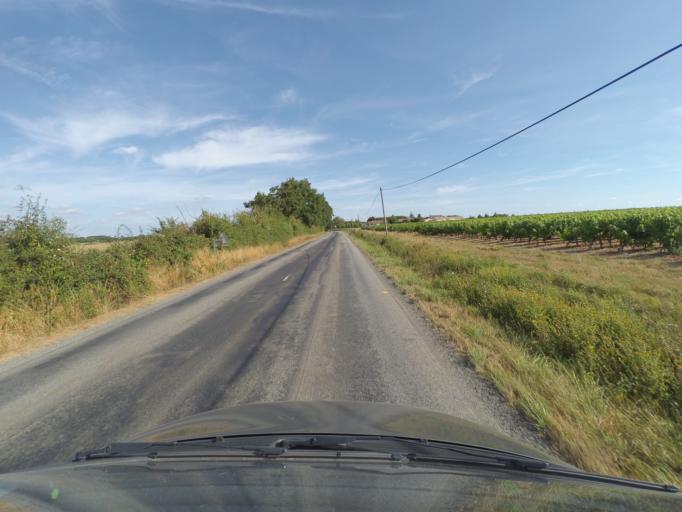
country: FR
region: Pays de la Loire
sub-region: Departement de la Loire-Atlantique
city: Vieillevigne
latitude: 46.9841
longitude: -1.4430
